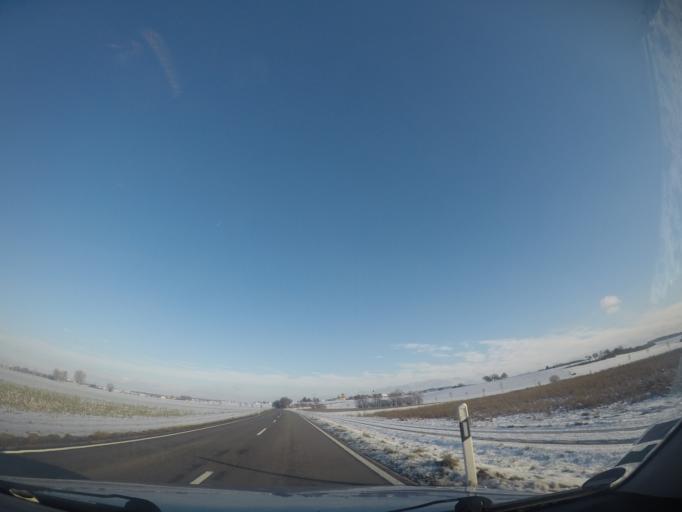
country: DE
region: Baden-Wuerttemberg
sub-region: Tuebingen Region
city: Dettingen
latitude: 48.2347
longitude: 9.7205
